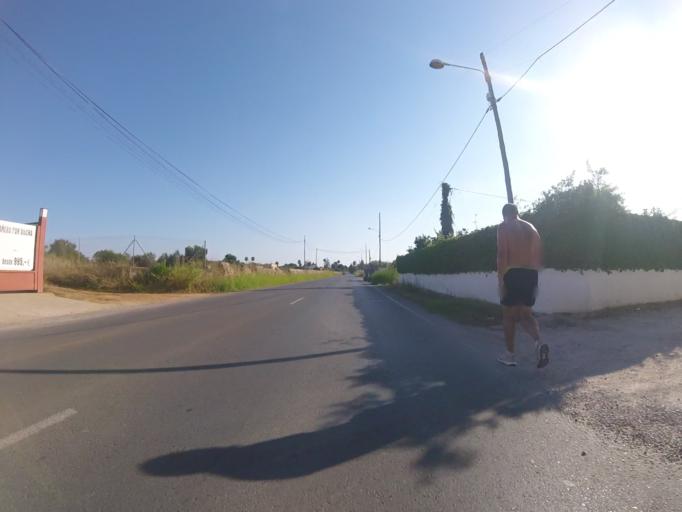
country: ES
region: Valencia
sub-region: Provincia de Castello
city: Benicarlo
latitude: 40.4063
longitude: 0.4168
